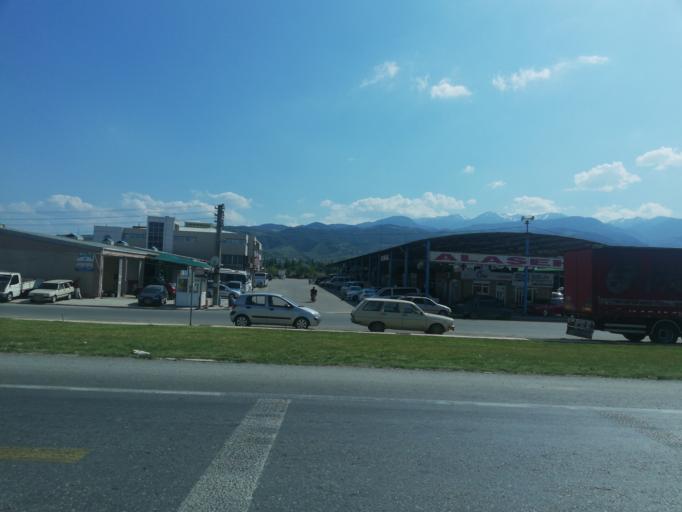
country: TR
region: Manisa
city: Alasehir
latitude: 38.3586
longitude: 28.5424
